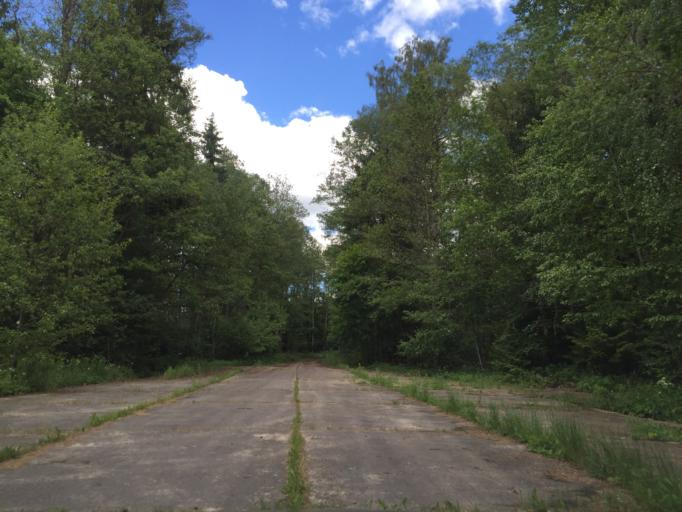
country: LV
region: Lecava
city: Iecava
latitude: 56.5501
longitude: 24.3489
